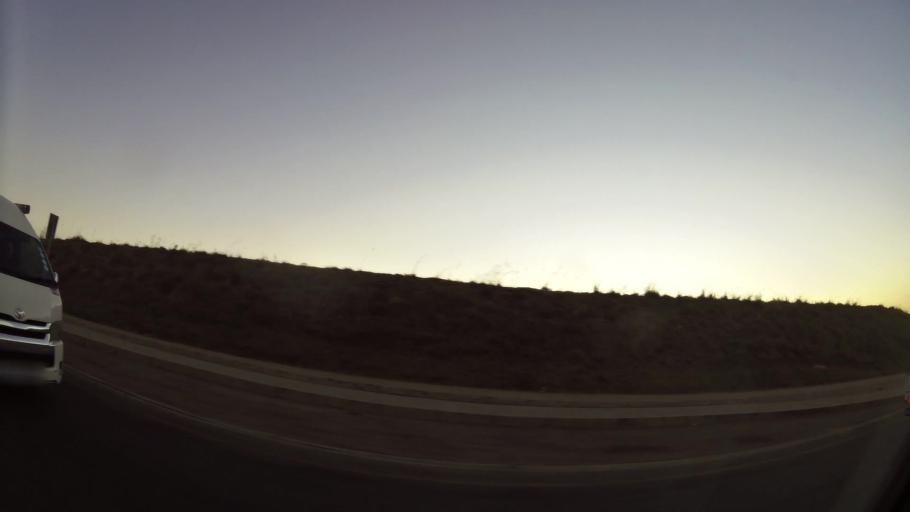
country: ZA
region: Gauteng
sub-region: City of Johannesburg Metropolitan Municipality
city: Diepsloot
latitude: -25.9693
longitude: 28.0251
